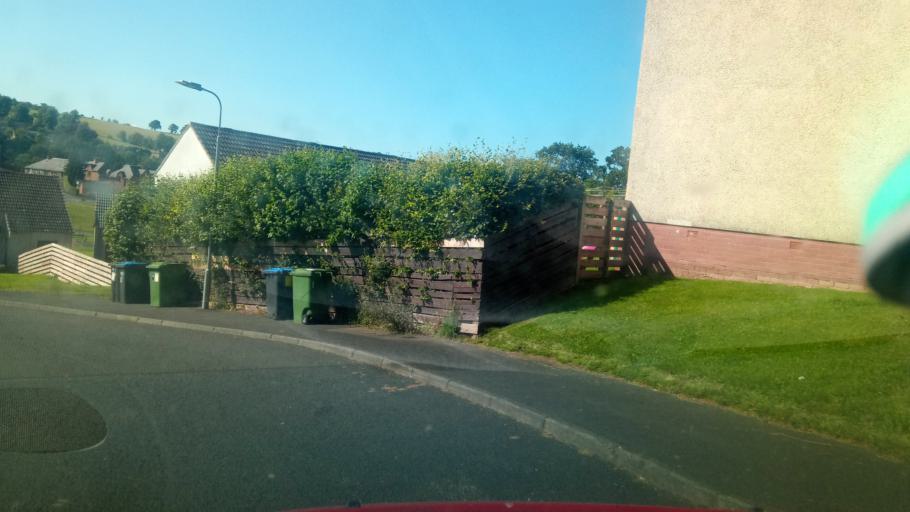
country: GB
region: Scotland
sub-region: The Scottish Borders
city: Jedburgh
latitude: 55.4807
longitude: -2.5448
